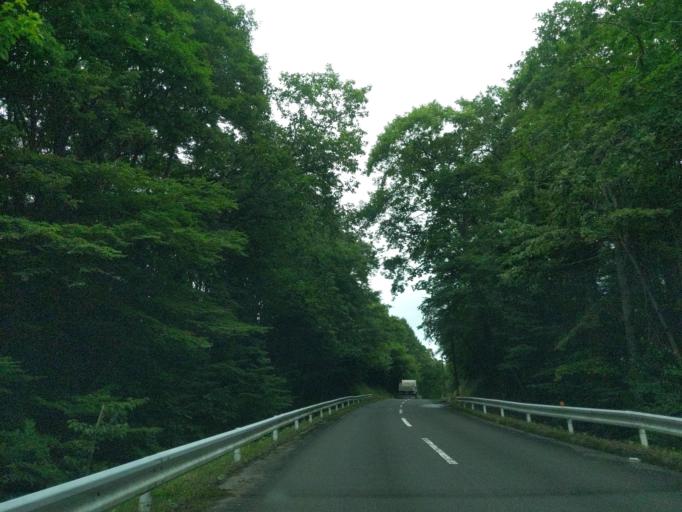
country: JP
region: Fukushima
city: Sukagawa
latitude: 37.2581
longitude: 140.0910
